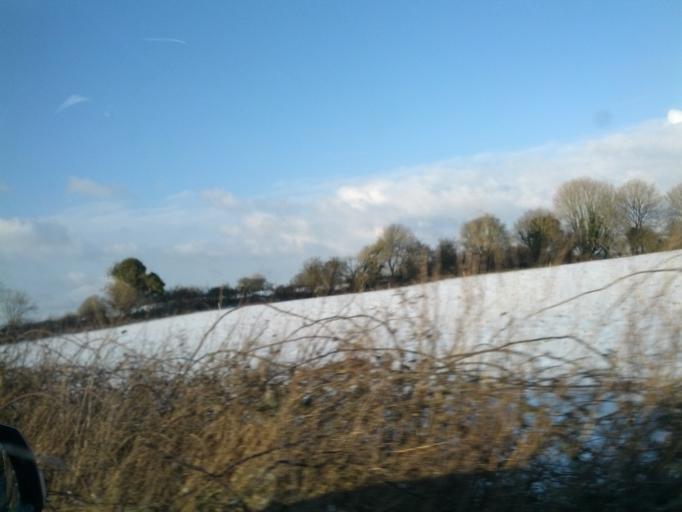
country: IE
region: Connaught
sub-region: County Galway
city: Athenry
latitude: 53.1858
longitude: -8.7228
